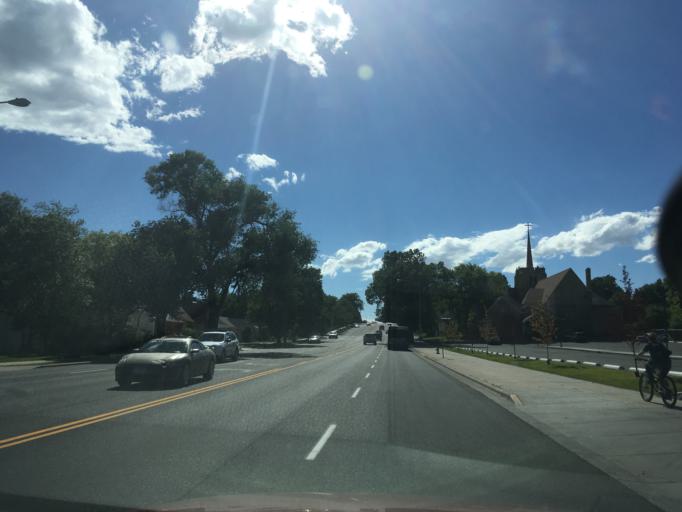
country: US
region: Montana
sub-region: Yellowstone County
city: Billings
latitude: 45.7841
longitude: -108.5284
